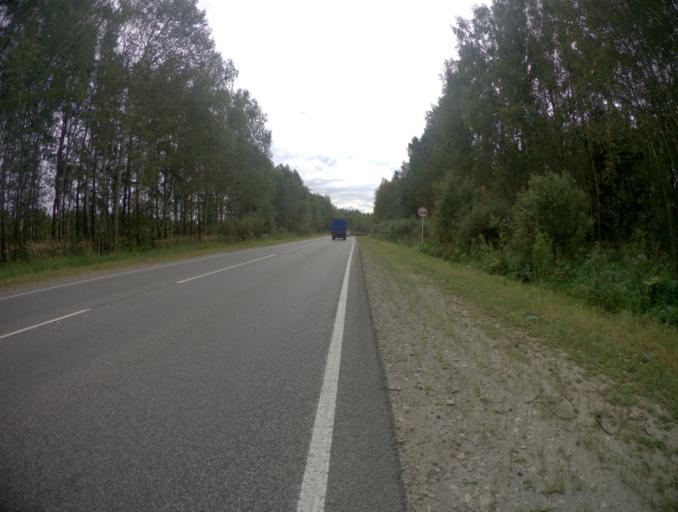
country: RU
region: Vladimir
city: Golovino
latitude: 55.9405
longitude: 40.5891
